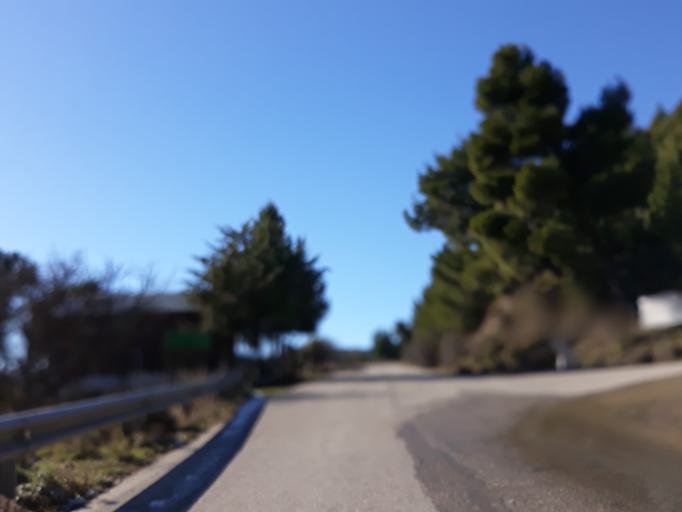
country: GR
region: Attica
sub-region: Nomarchia Dytikis Attikis
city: Fyli
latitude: 38.1451
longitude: 23.6432
